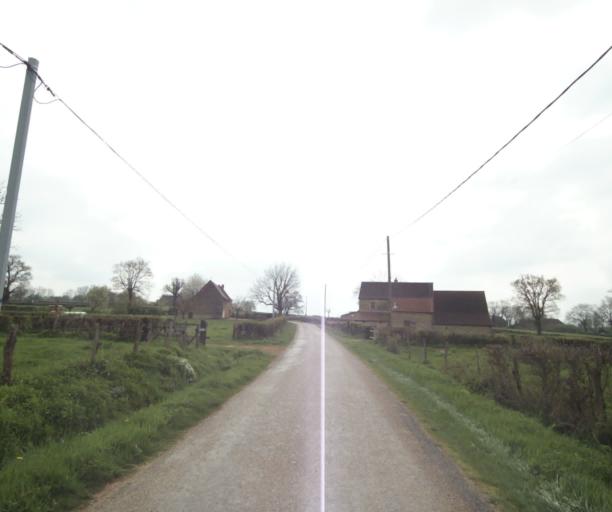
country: FR
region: Bourgogne
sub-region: Departement de Saone-et-Loire
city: Charolles
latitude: 46.3589
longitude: 4.2197
